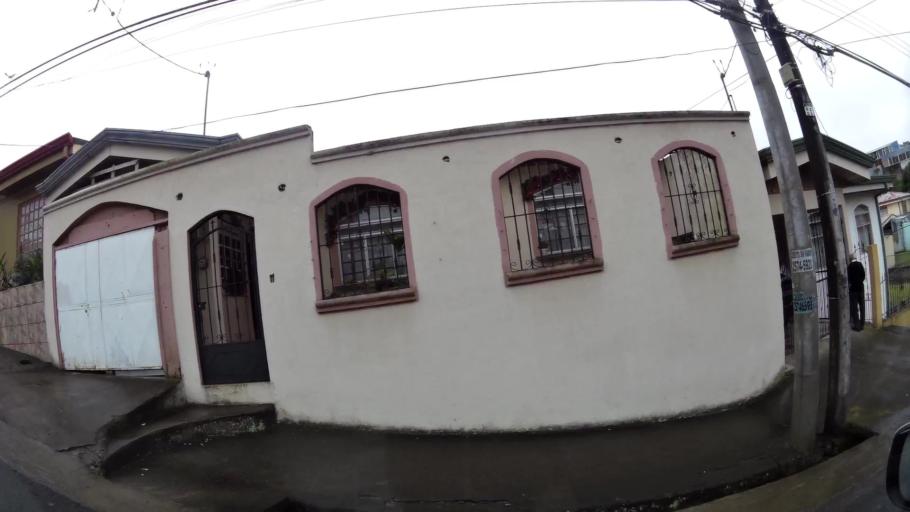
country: CR
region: Cartago
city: Paraiso
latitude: 9.8386
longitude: -83.8690
